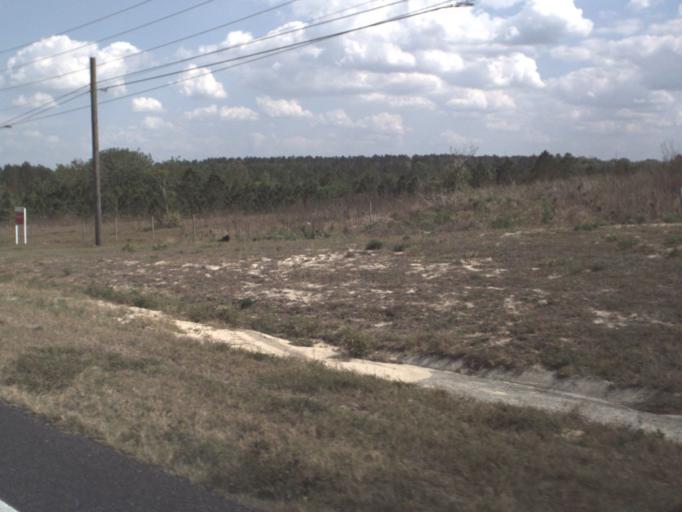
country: US
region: Florida
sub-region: Lake County
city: Howie In The Hills
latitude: 28.6453
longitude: -81.8204
